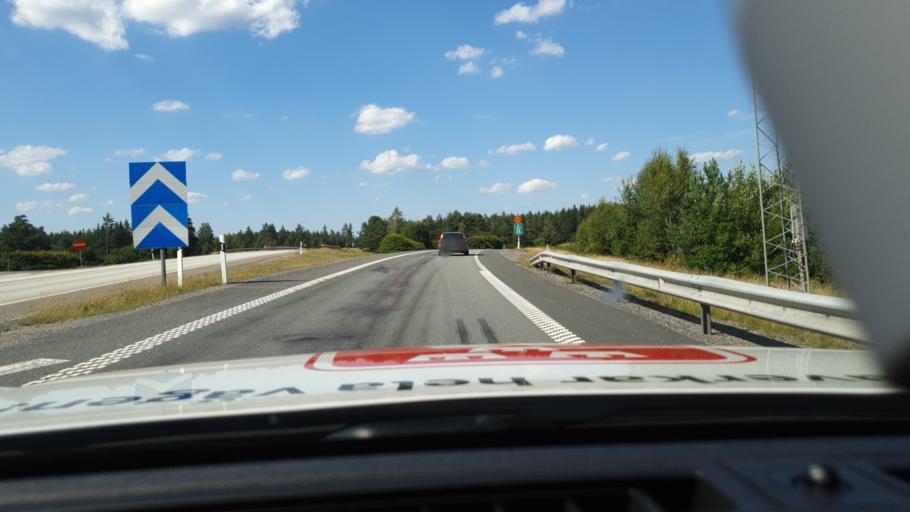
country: SE
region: Joenkoeping
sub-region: Jonkopings Kommun
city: Odensjo
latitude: 57.6246
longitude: 14.1868
